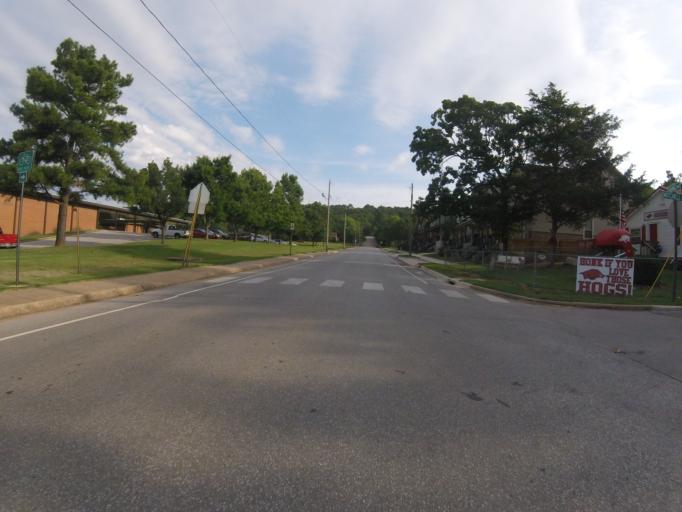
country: US
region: Arkansas
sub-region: Washington County
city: Fayetteville
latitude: 36.0582
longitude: -94.1893
